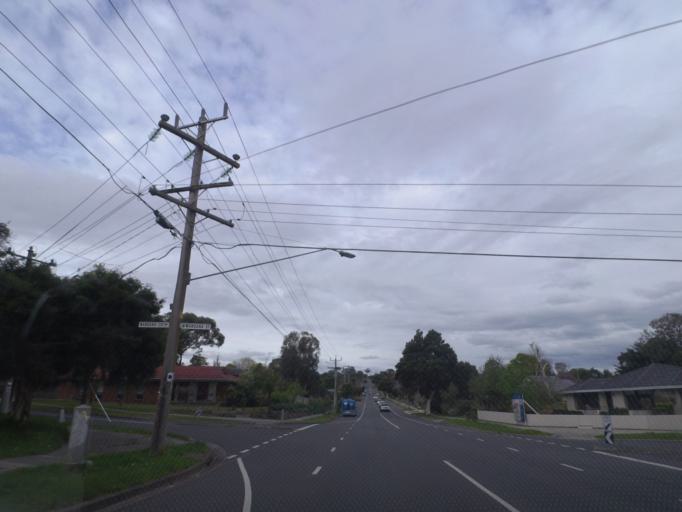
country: AU
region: Victoria
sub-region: Maroondah
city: Croydon North
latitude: -37.7728
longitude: 145.3063
